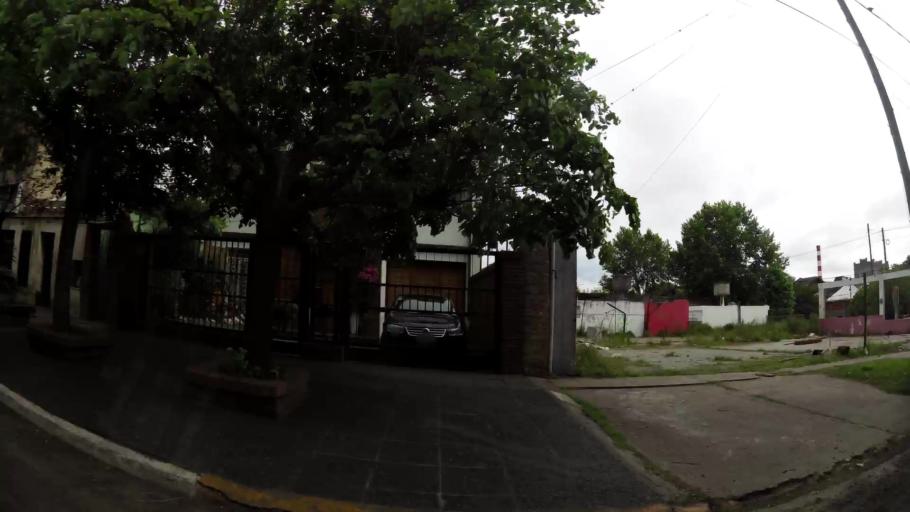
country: AR
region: Buenos Aires
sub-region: Partido de Quilmes
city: Quilmes
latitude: -34.7327
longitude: -58.2602
